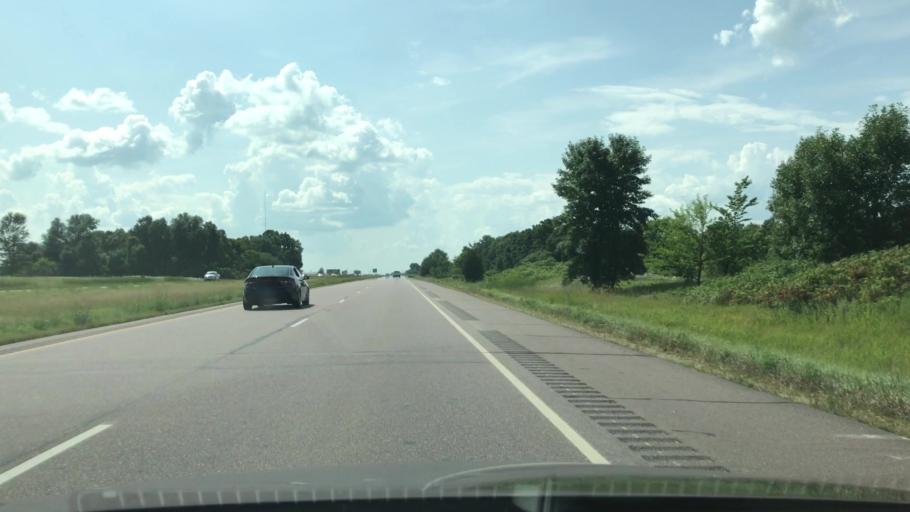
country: US
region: Minnesota
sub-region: Nicollet County
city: North Mankato
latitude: 44.1447
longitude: -94.0974
